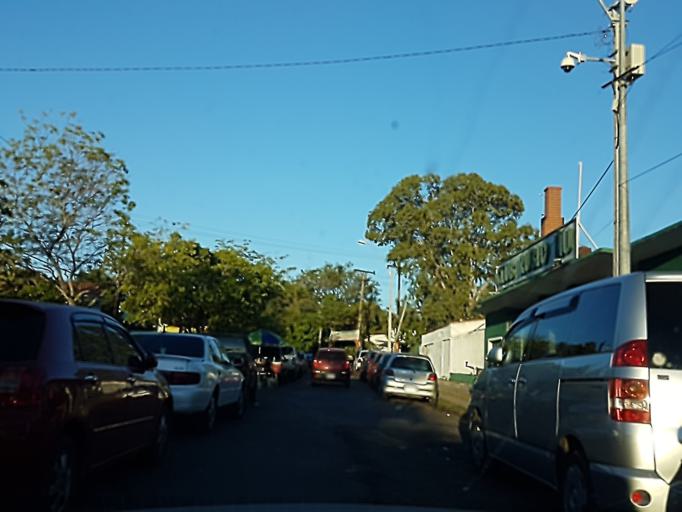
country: PY
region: Asuncion
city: Asuncion
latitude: -25.2568
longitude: -57.5760
